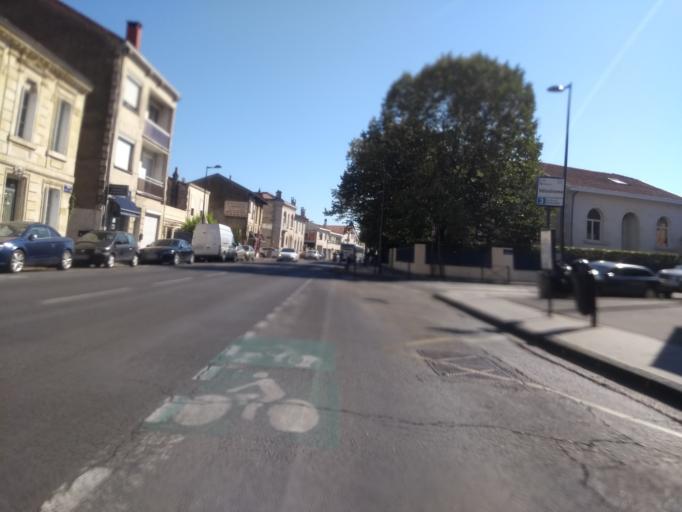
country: FR
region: Aquitaine
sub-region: Departement de la Gironde
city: Le Bouscat
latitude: 44.8530
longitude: -0.6094
